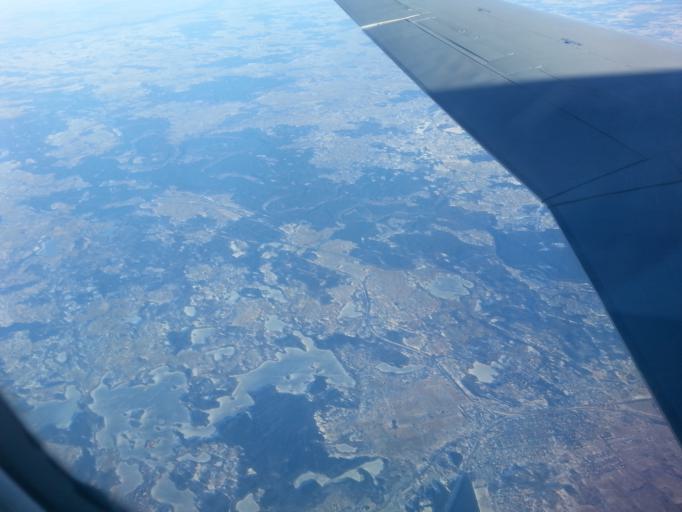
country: LT
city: Trakai
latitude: 54.5829
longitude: 24.9752
